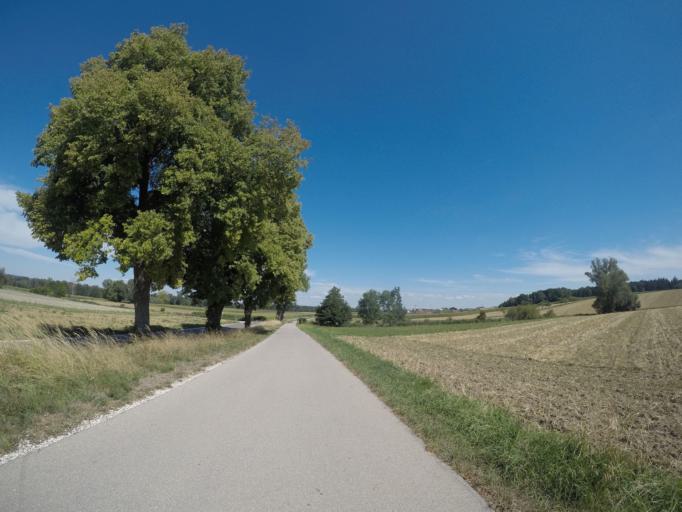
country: DE
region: Bavaria
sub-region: Swabia
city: Holzheim
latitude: 48.3679
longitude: 10.0706
